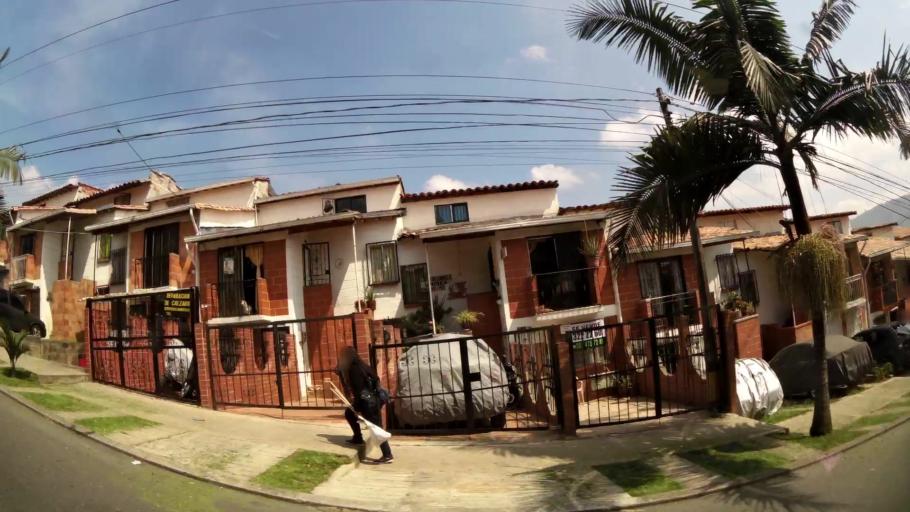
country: CO
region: Antioquia
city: La Estrella
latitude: 6.1749
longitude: -75.6523
